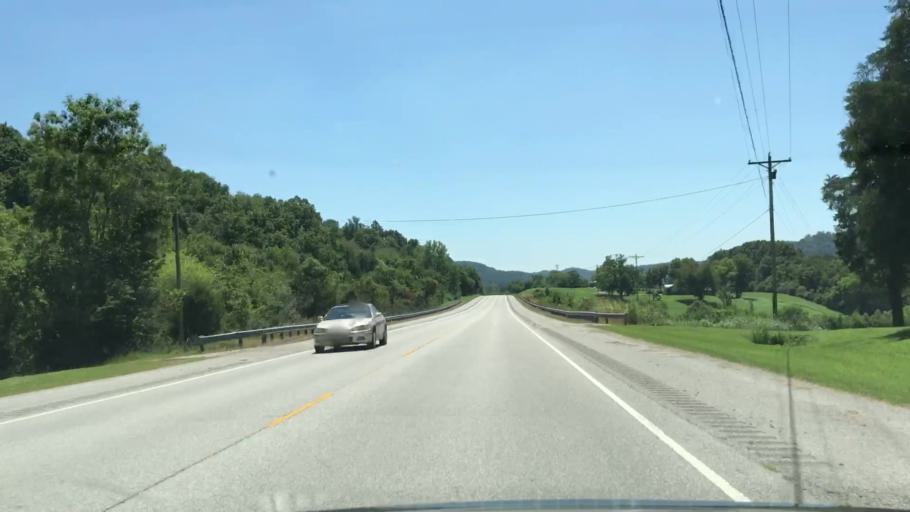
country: US
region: Tennessee
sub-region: Jackson County
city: Gainesboro
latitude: 36.4201
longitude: -85.6397
